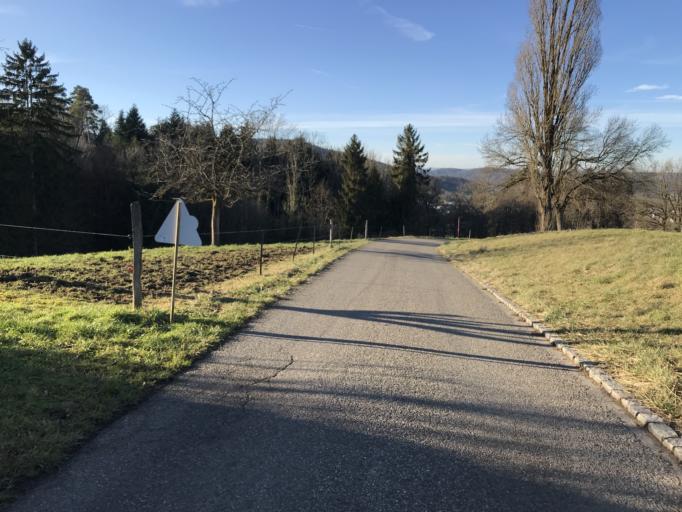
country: CH
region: Thurgau
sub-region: Frauenfeld District
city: Wagenhausen
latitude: 47.6435
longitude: 8.8513
